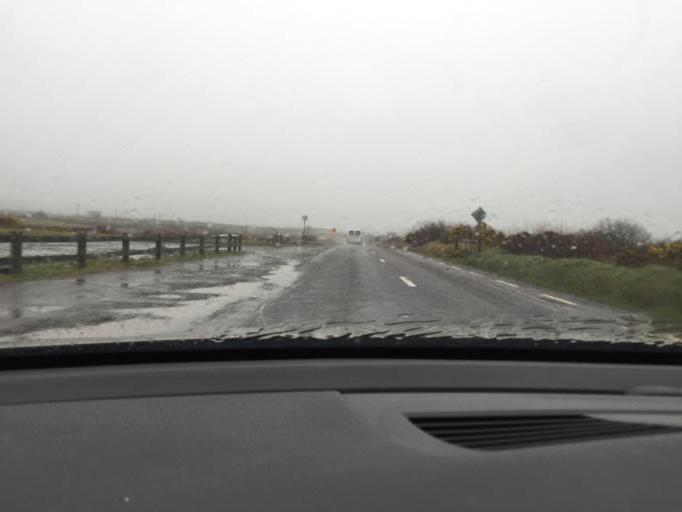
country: IE
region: Munster
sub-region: Ciarrai
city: Dingle
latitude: 52.1403
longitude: -10.2169
